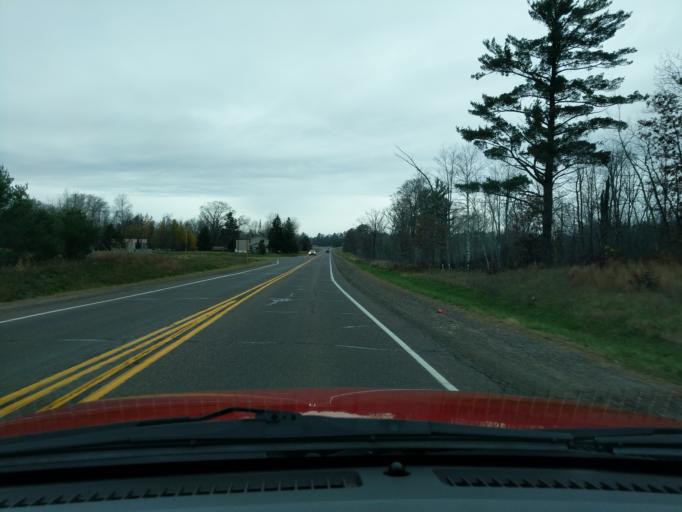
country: US
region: Wisconsin
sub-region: Washburn County
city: Spooner
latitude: 45.8191
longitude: -91.8607
